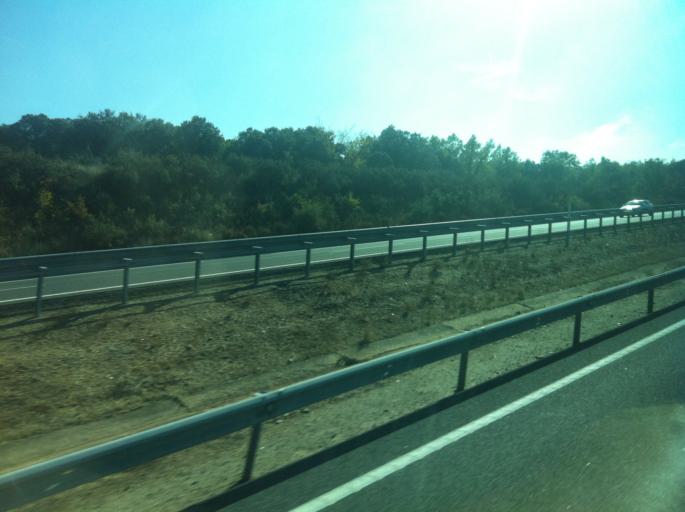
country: ES
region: Castille and Leon
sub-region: Provincia de Burgos
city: Madrigalejo del Monte
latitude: 42.1022
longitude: -3.7221
